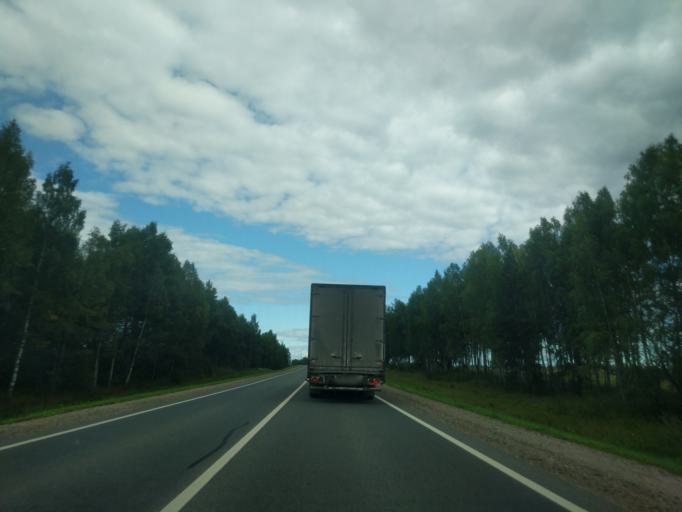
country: RU
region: Kostroma
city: Ostrovskoye
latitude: 57.8154
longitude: 42.2156
